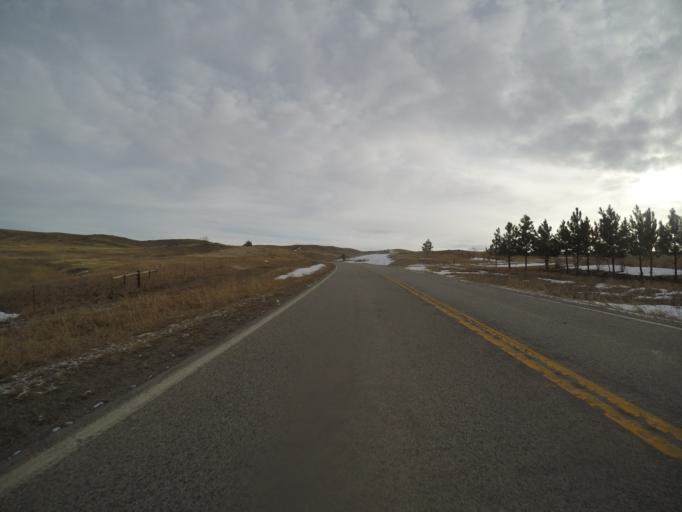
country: US
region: Montana
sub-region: Stillwater County
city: Absarokee
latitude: 45.3186
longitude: -109.4490
